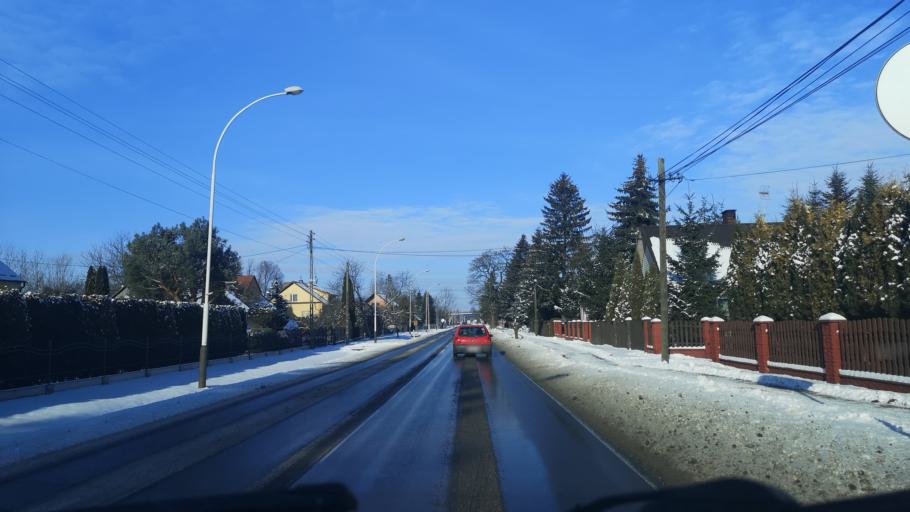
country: PL
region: Subcarpathian Voivodeship
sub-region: Powiat przeworski
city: Przeworsk
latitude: 50.0749
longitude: 22.4937
